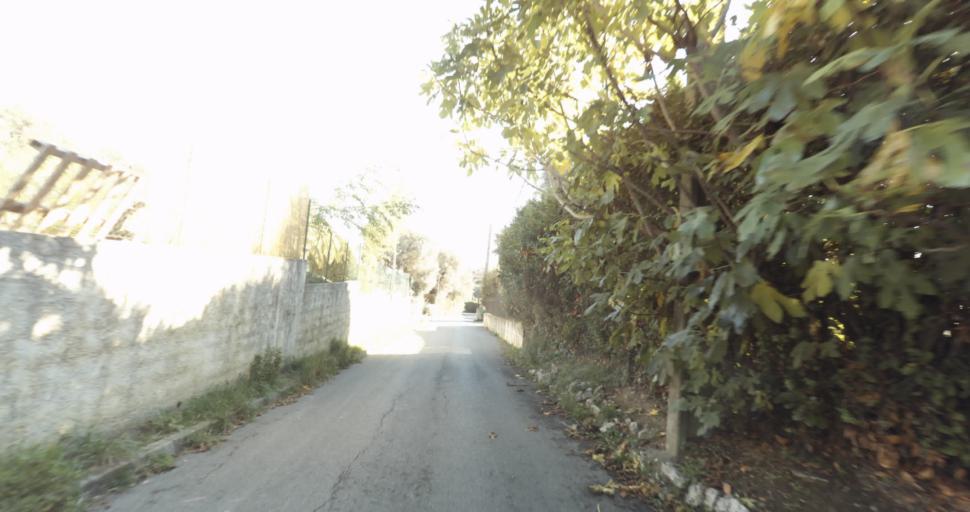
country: FR
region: Provence-Alpes-Cote d'Azur
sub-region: Departement des Alpes-Maritimes
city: Saint-Paul-de-Vence
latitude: 43.7037
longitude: 7.1341
